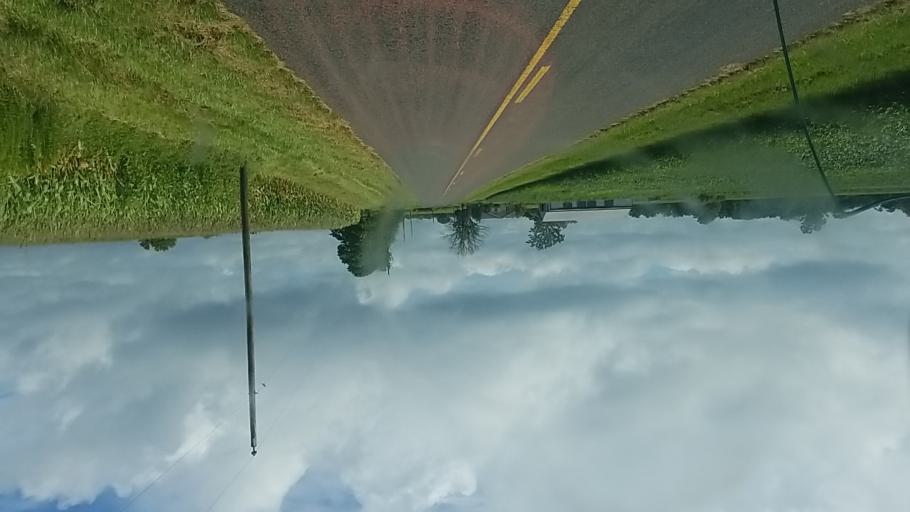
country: US
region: Ohio
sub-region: Hardin County
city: Kenton
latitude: 40.4905
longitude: -83.5173
